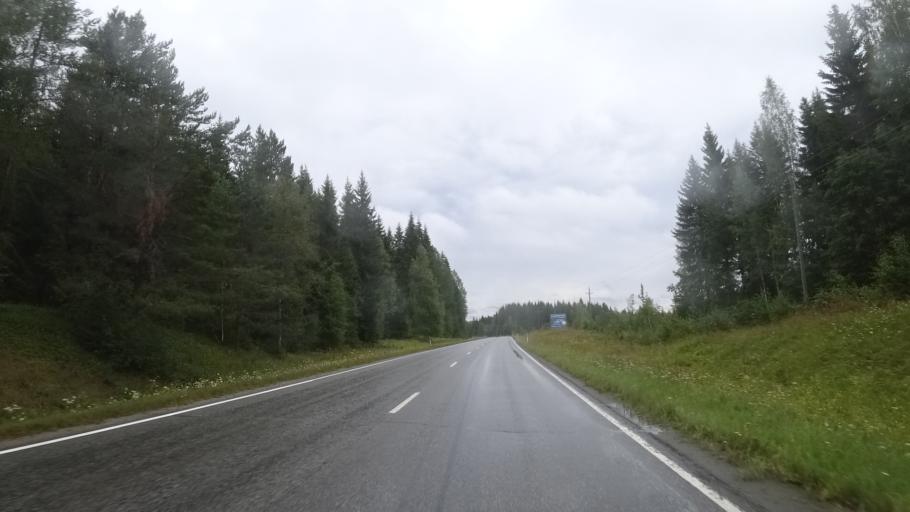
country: FI
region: Southern Savonia
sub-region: Savonlinna
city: Kerimaeki
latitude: 61.9853
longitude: 29.2820
